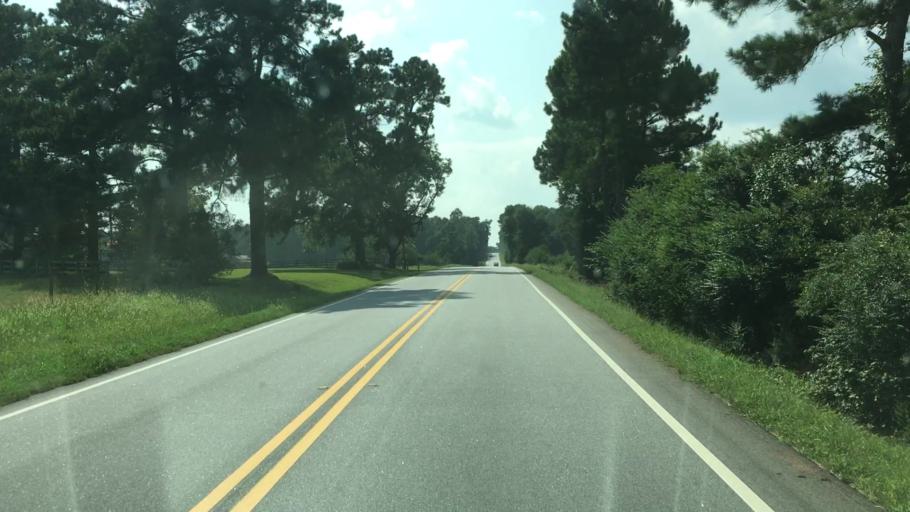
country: US
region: Georgia
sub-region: Jasper County
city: Monticello
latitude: 33.3545
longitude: -83.7339
